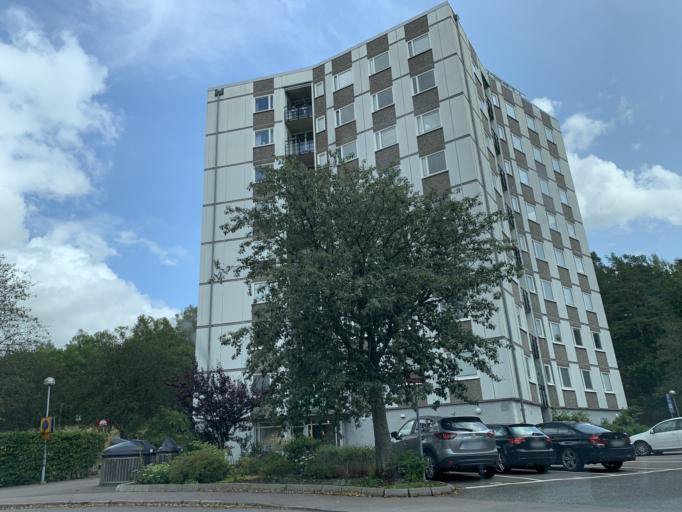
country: SE
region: Vaestra Goetaland
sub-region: Goteborg
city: Eriksbo
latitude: 57.7606
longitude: 12.0604
